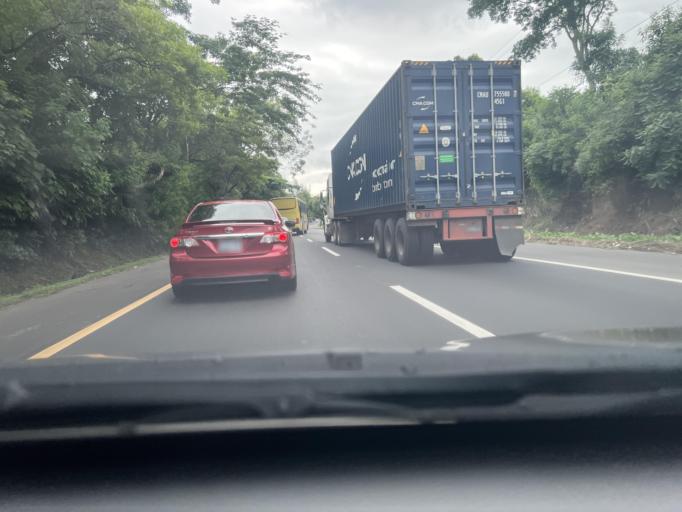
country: SV
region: Santa Ana
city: El Congo
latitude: 13.8795
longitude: -89.4906
